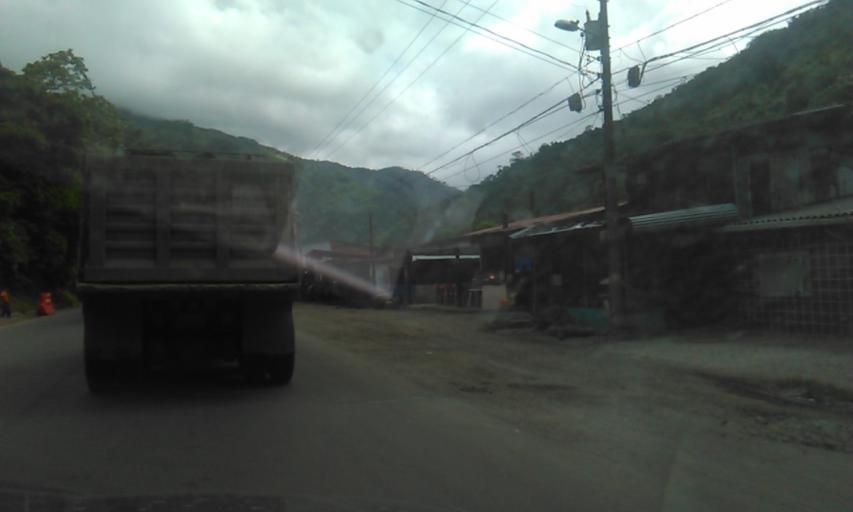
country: CO
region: Valle del Cauca
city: Dagua
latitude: 3.7842
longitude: -76.7607
